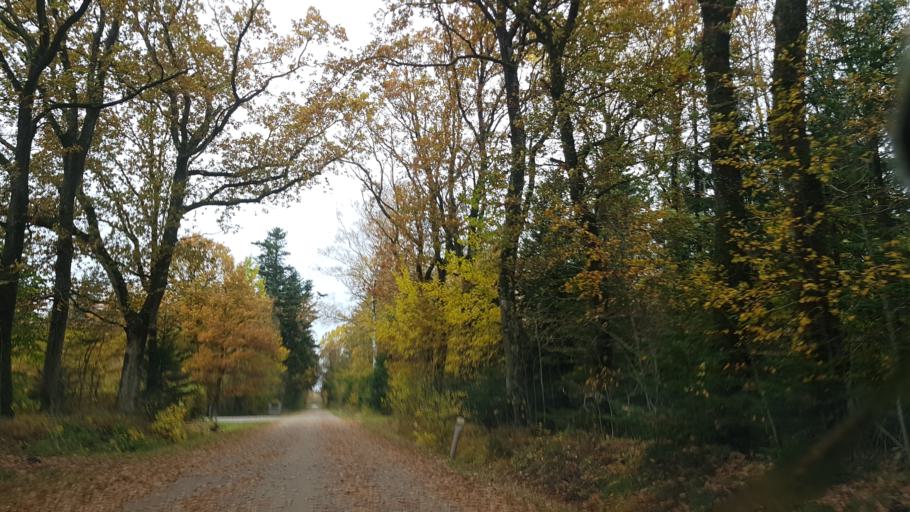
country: DK
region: South Denmark
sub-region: Tonder Kommune
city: Sherrebek
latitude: 55.1849
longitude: 8.7644
